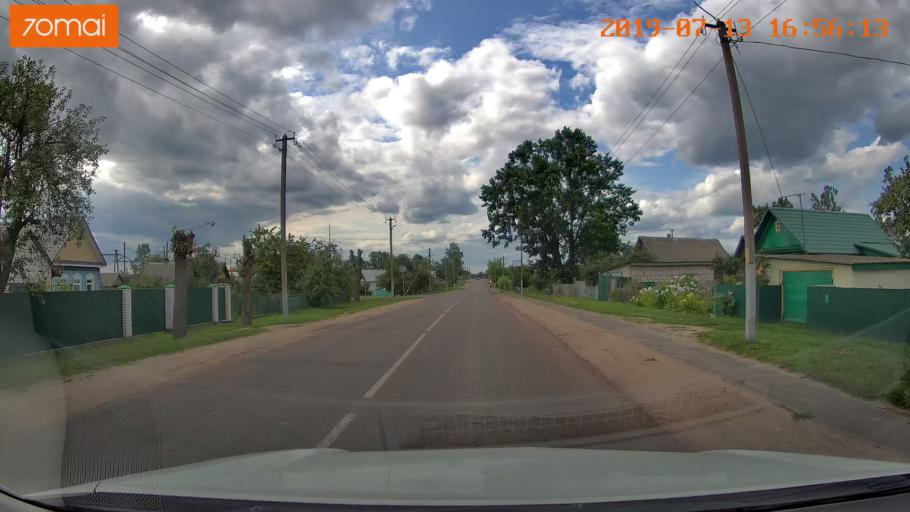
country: BY
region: Mogilev
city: Kirawsk
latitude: 53.2720
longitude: 29.4607
